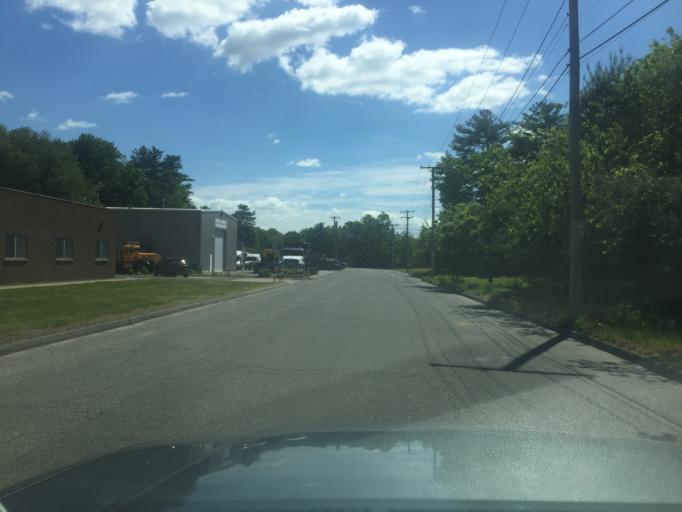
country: US
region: Massachusetts
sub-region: Norfolk County
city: Medway
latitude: 42.1591
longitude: -71.3923
